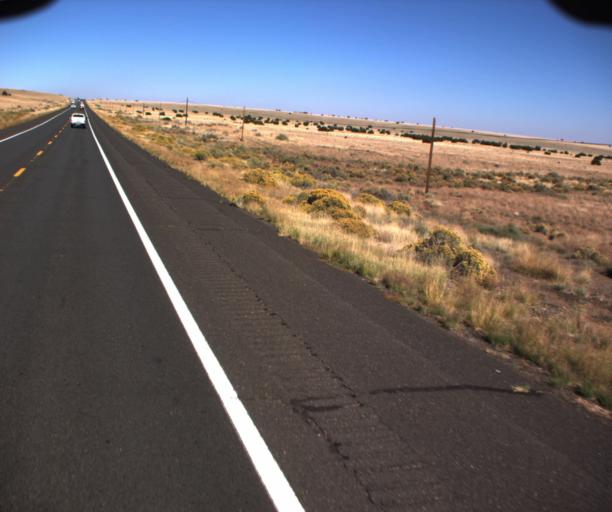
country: US
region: Arizona
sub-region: Coconino County
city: Flagstaff
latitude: 35.5573
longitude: -111.5351
